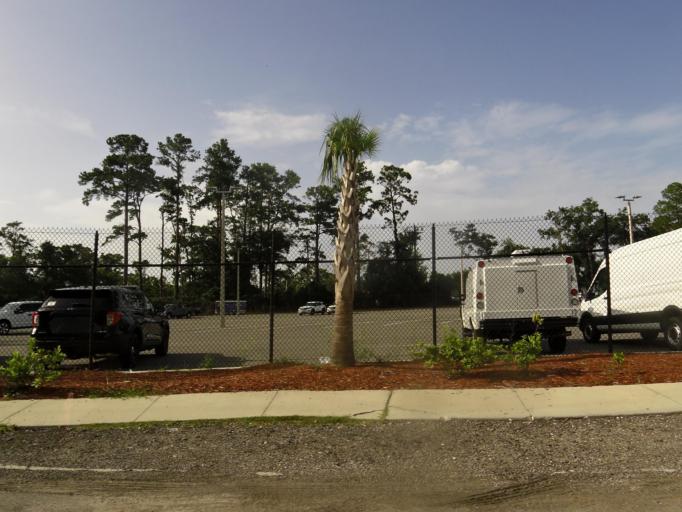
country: US
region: Florida
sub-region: Duval County
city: Jacksonville
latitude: 30.2893
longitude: -81.7366
